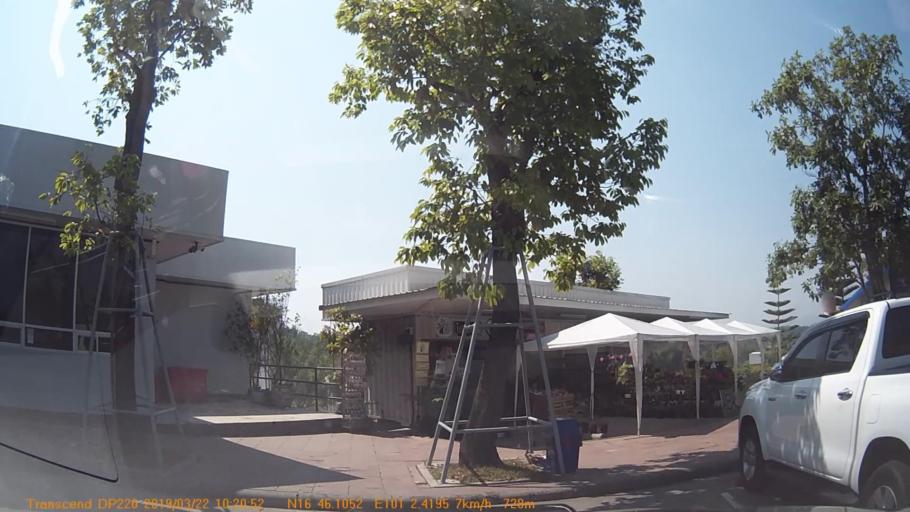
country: TH
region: Phetchabun
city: Khao Kho
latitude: 16.7684
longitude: 101.0403
